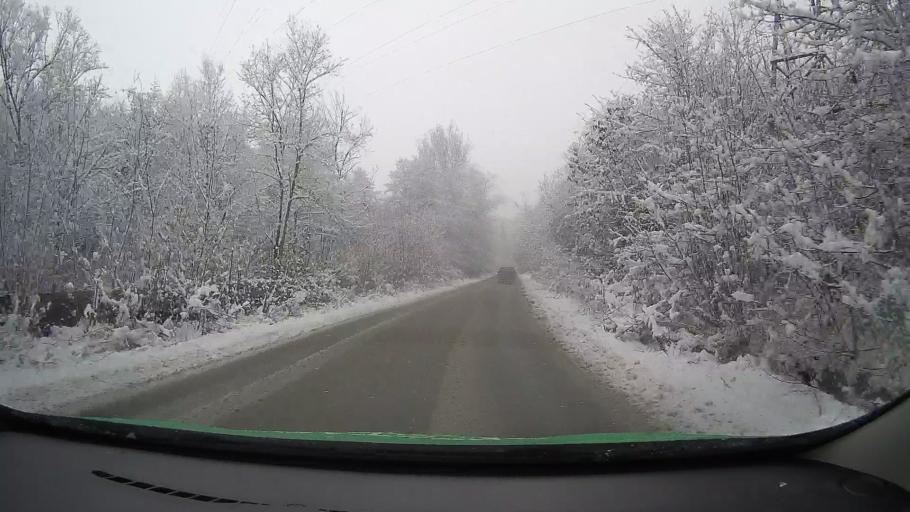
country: RO
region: Hunedoara
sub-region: Comuna Teliucu Inferior
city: Teliucu Inferior
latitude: 45.7295
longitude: 22.8820
